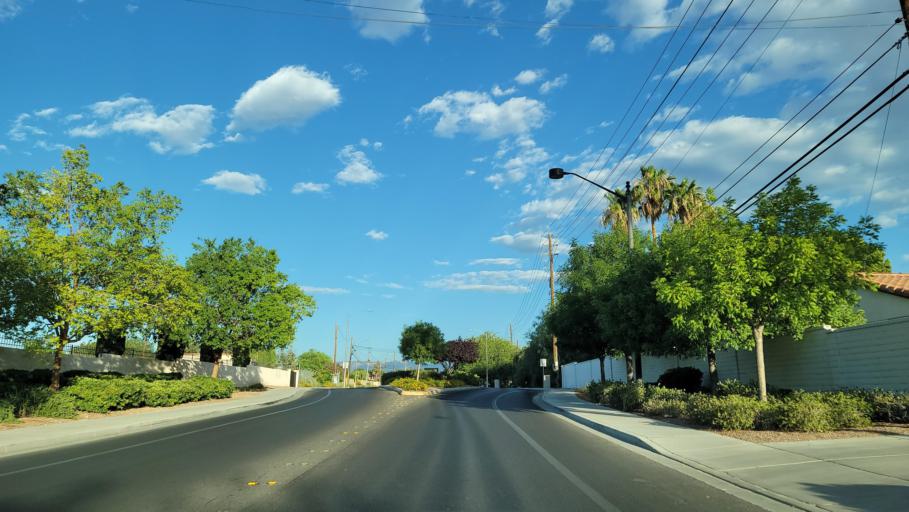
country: US
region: Nevada
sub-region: Clark County
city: Las Vegas
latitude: 36.1663
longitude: -115.1872
